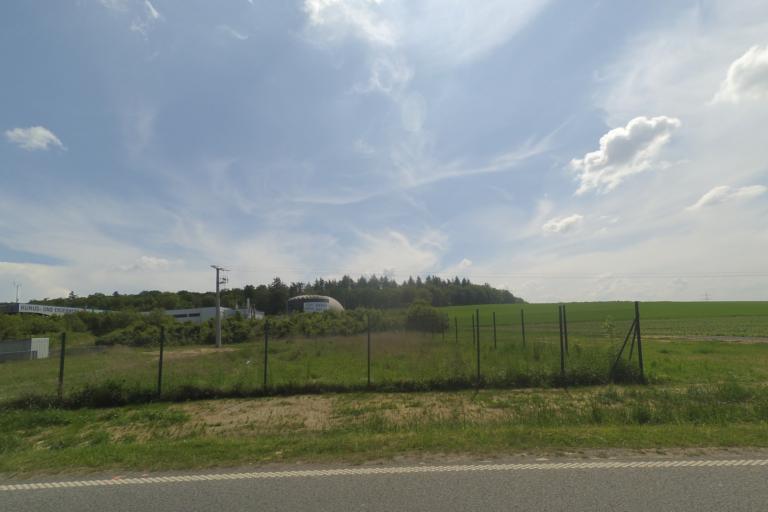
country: DE
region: Hesse
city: Nidderau
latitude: 50.2732
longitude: 8.8255
